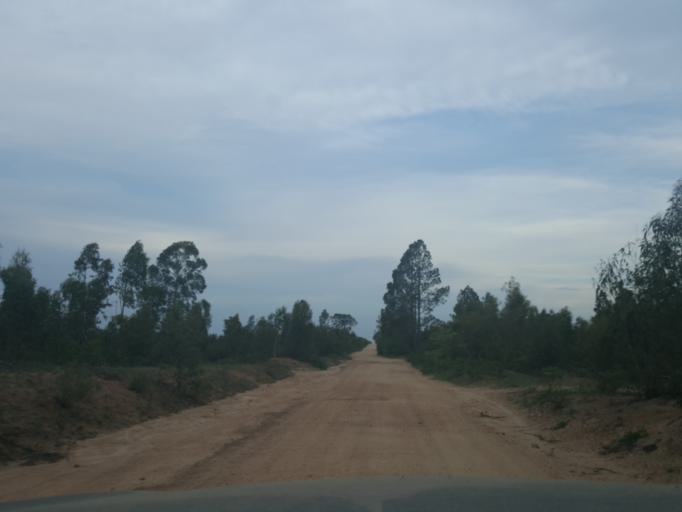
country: ZA
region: Limpopo
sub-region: Mopani District Municipality
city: Hoedspruit
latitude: -24.5865
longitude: 30.9713
